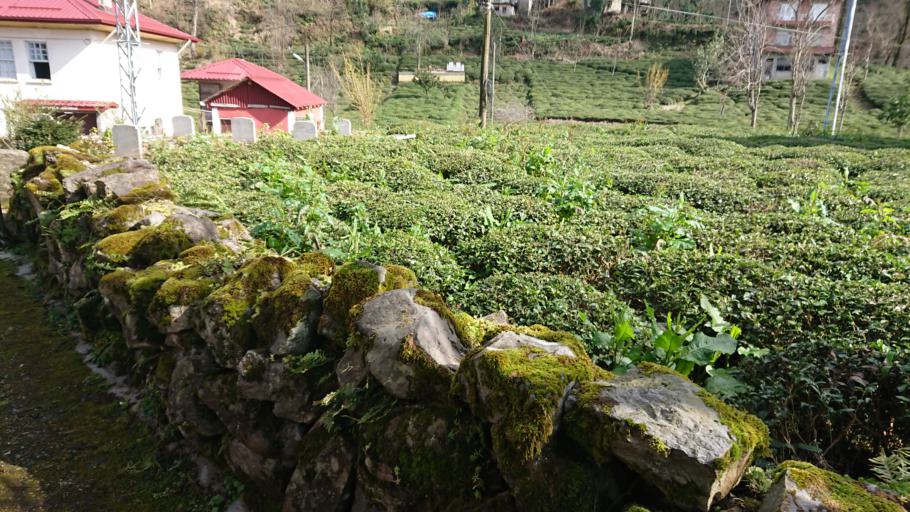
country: TR
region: Rize
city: Rize
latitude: 40.9811
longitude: 40.4950
